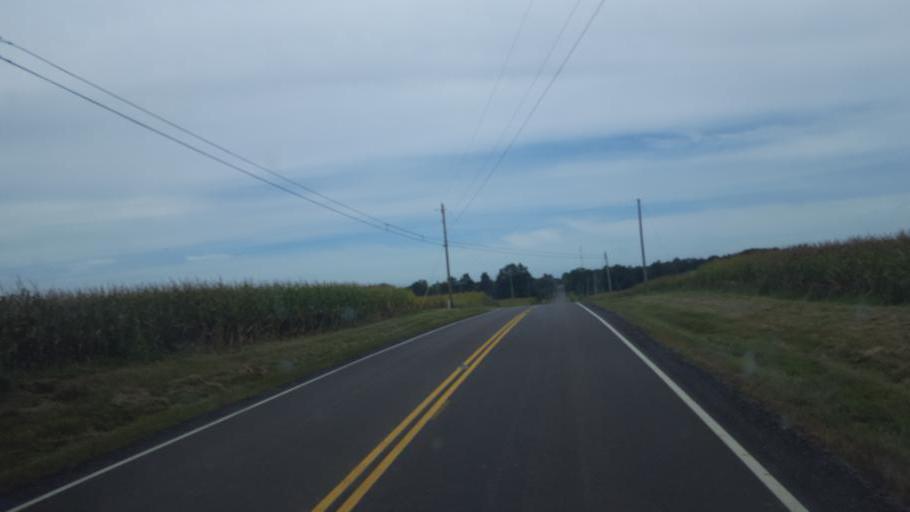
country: US
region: Ohio
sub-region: Knox County
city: Centerburg
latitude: 40.3374
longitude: -82.6905
